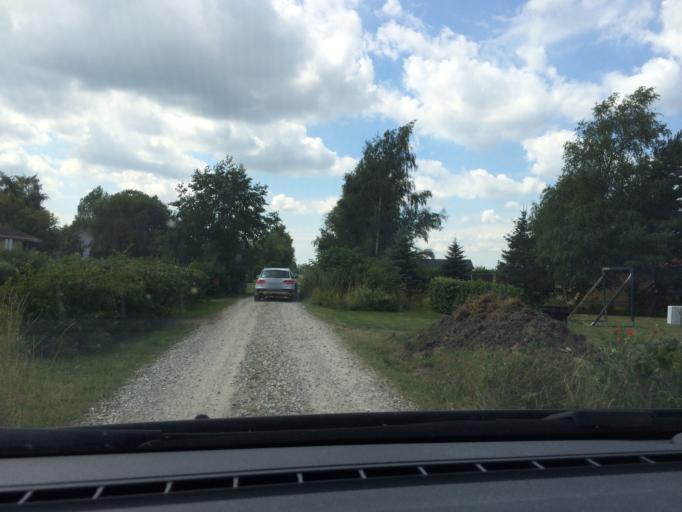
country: DK
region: Zealand
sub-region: Vordingborg Kommune
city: Stege
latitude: 55.0307
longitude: 12.2882
